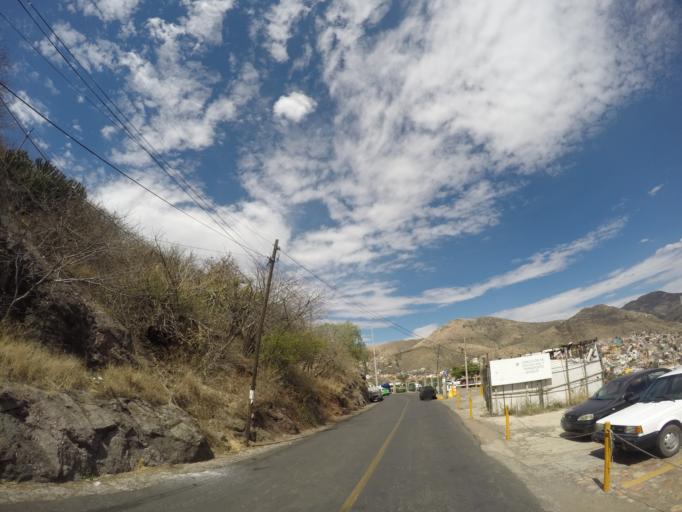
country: MX
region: Guanajuato
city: Guanajuato
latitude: 21.0131
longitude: -101.2550
